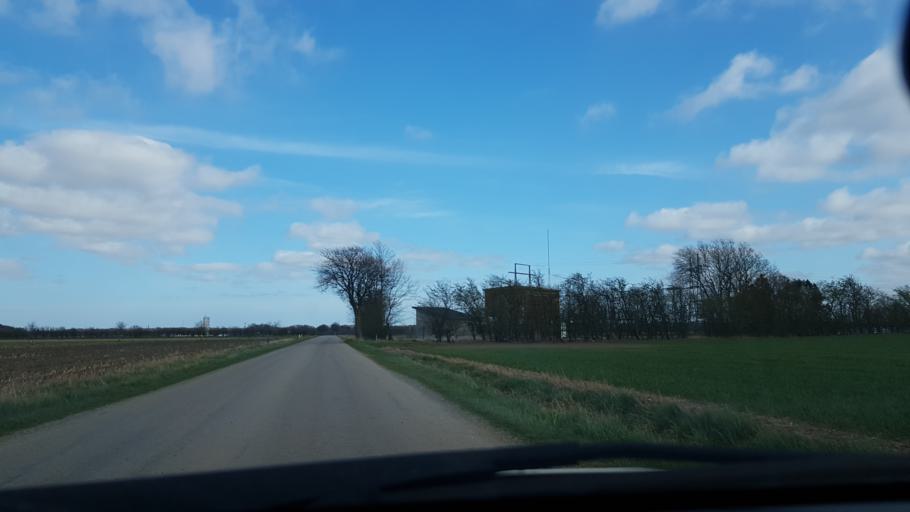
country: DK
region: South Denmark
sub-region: Vejen Kommune
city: Vejen
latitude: 55.4245
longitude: 9.1263
